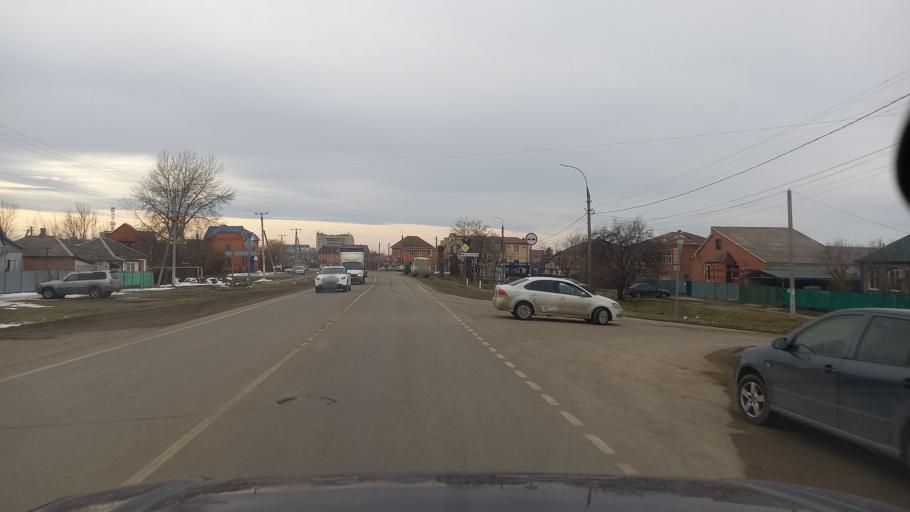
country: RU
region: Krasnodarskiy
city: Belorechensk
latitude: 44.7680
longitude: 39.8789
